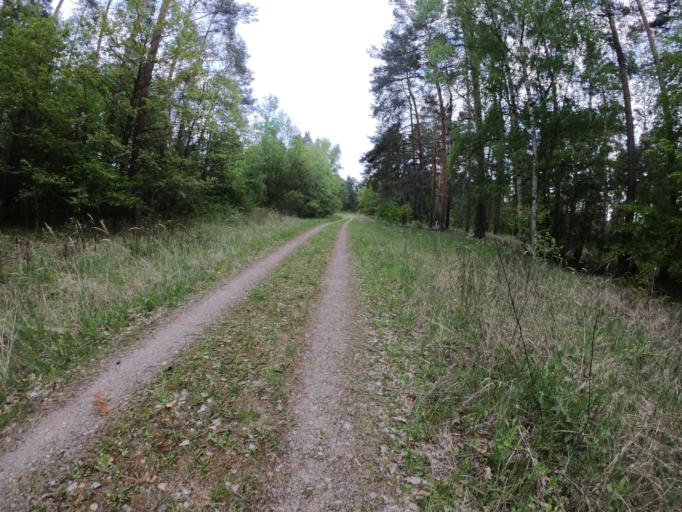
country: DE
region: Bavaria
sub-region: Upper Franconia
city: Memmelsdorf
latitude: 49.9170
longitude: 10.9379
